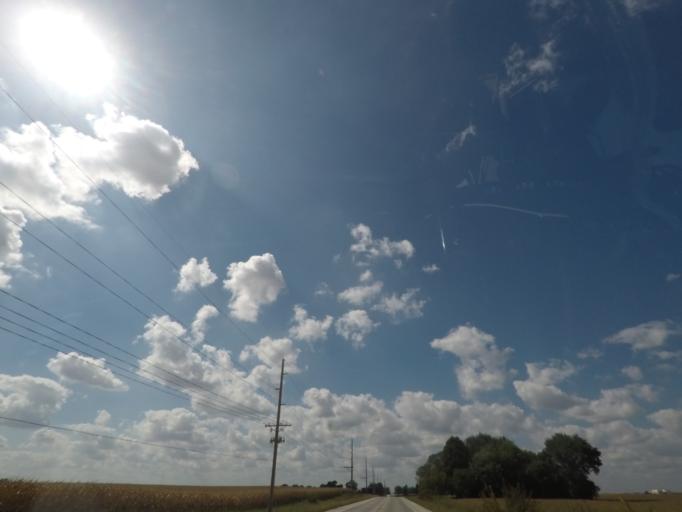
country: US
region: Iowa
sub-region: Story County
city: Nevada
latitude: 42.0231
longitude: -93.5326
